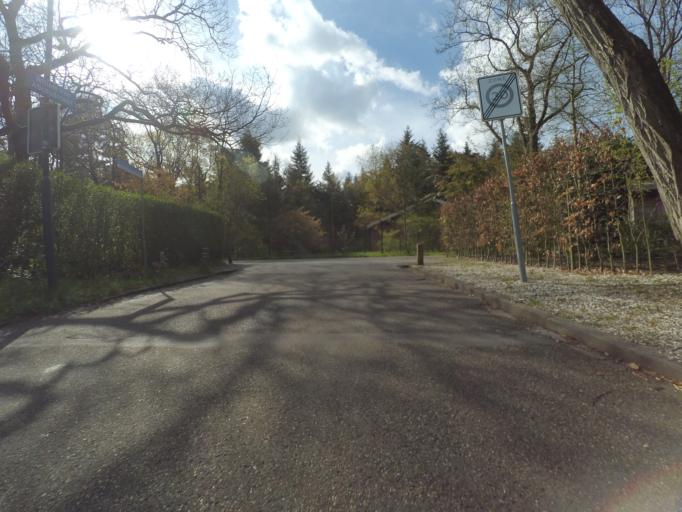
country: NL
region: Utrecht
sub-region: Gemeente Utrechtse Heuvelrug
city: Driebergen-Rijsenburg
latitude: 52.0609
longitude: 5.3058
